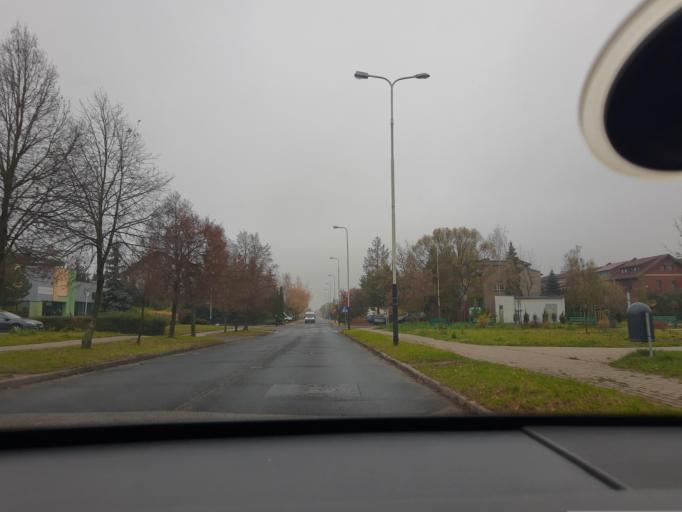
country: PL
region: Lodz Voivodeship
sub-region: Powiat pabianicki
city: Konstantynow Lodzki
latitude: 51.7423
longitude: 19.3785
